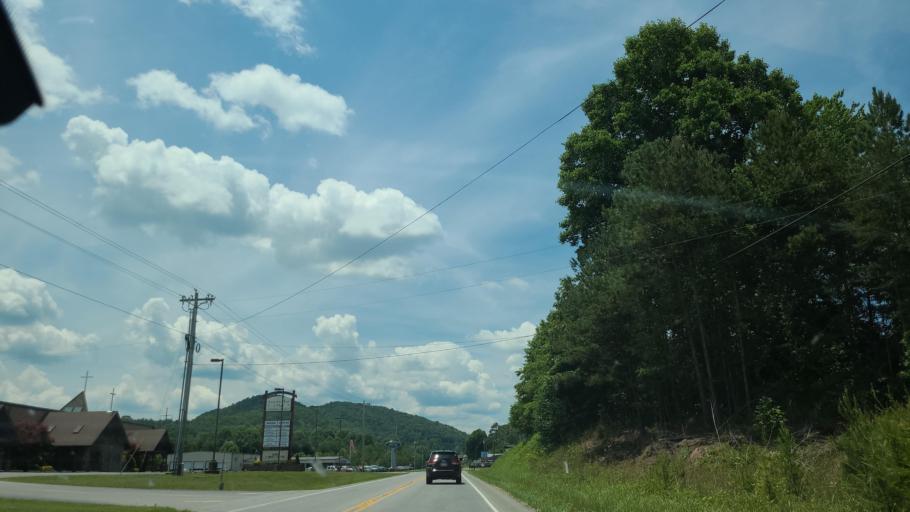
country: US
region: North Carolina
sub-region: Clay County
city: Hayesville
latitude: 35.0342
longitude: -83.8435
